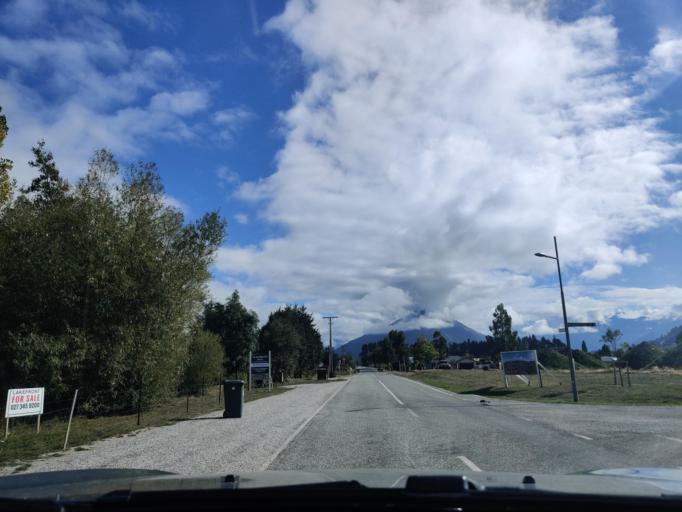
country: NZ
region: Otago
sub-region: Queenstown-Lakes District
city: Queenstown
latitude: -44.8548
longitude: 168.3902
